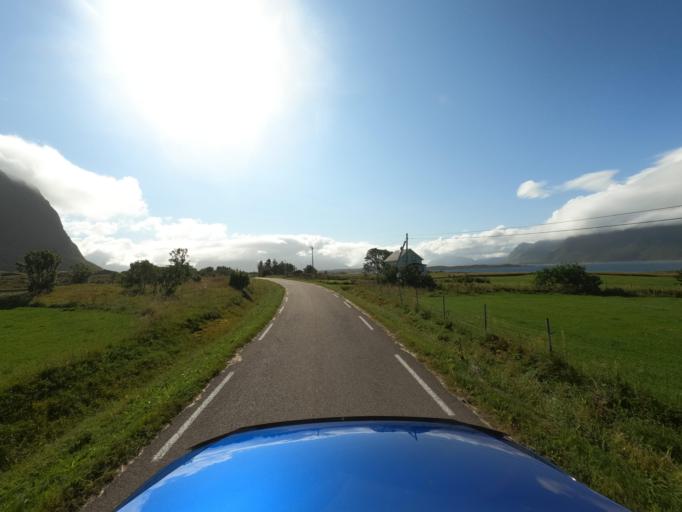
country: NO
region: Nordland
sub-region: Vestvagoy
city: Evjen
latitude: 68.3396
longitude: 14.0840
